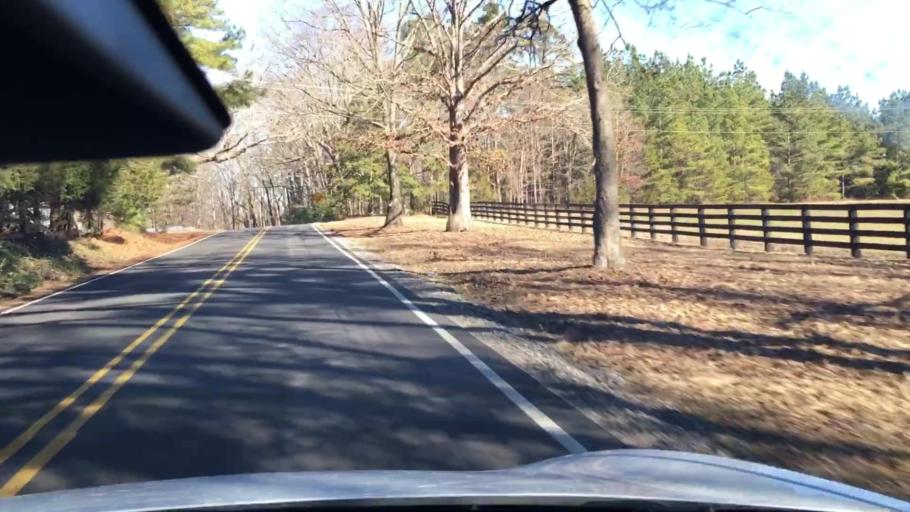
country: US
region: Virginia
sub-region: Powhatan County
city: Powhatan
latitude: 37.5770
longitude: -77.7733
